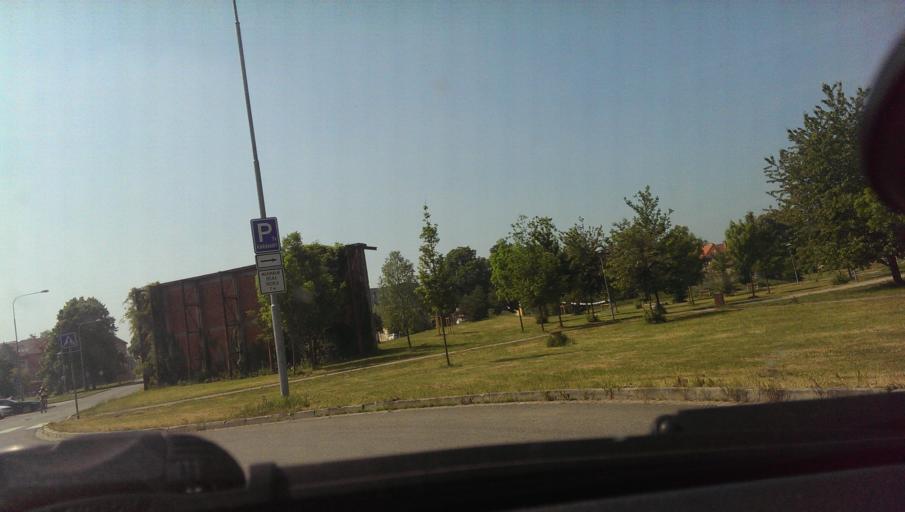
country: CZ
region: Zlin
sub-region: Okres Uherske Hradiste
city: Uherske Hradiste
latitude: 49.0718
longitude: 17.4708
